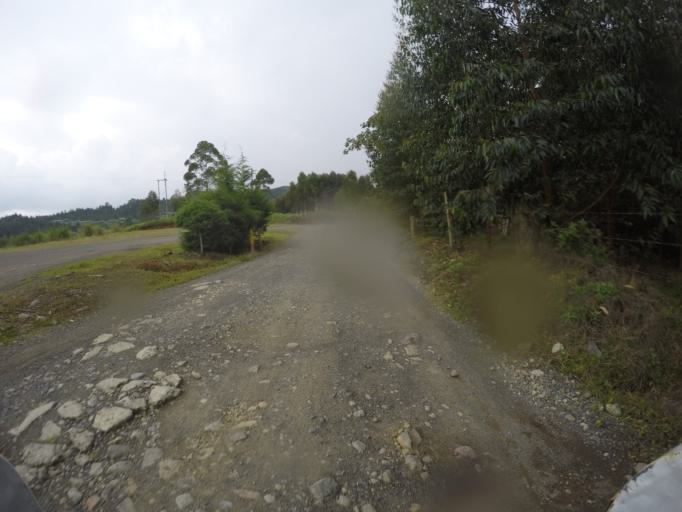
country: CO
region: Quindio
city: Filandia
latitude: 4.7124
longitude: -75.6325
